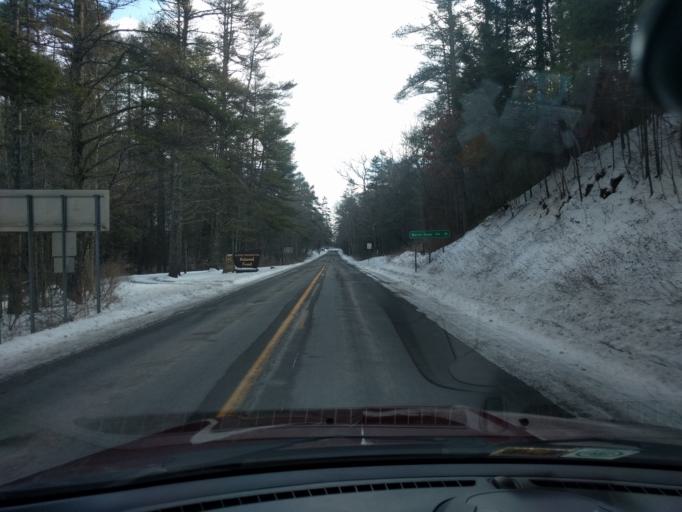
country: US
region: West Virginia
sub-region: Pocahontas County
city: Marlinton
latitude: 38.1244
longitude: -79.9491
